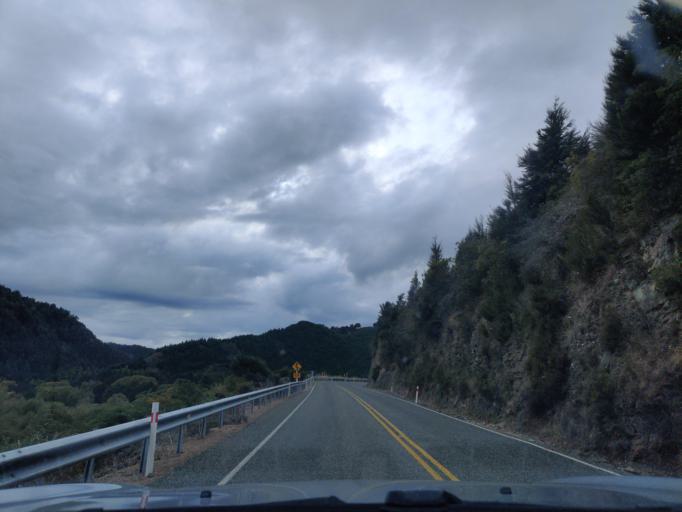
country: NZ
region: Tasman
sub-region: Tasman District
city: Wakefield
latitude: -41.7034
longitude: 172.6652
